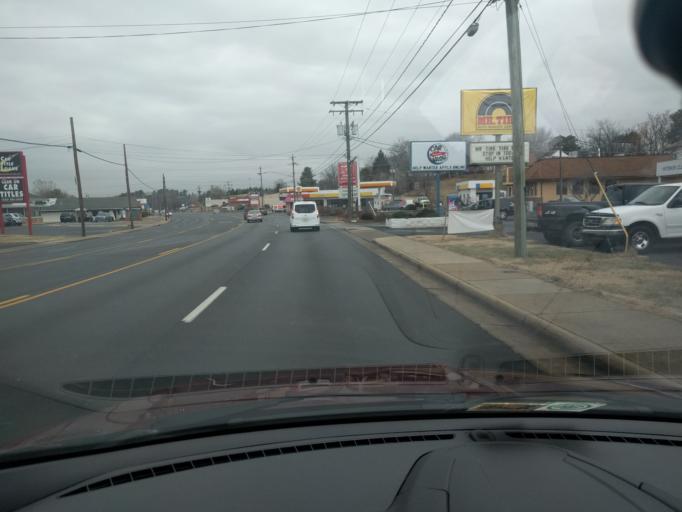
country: US
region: Virginia
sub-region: City of Staunton
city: Staunton
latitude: 38.1336
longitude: -79.0636
